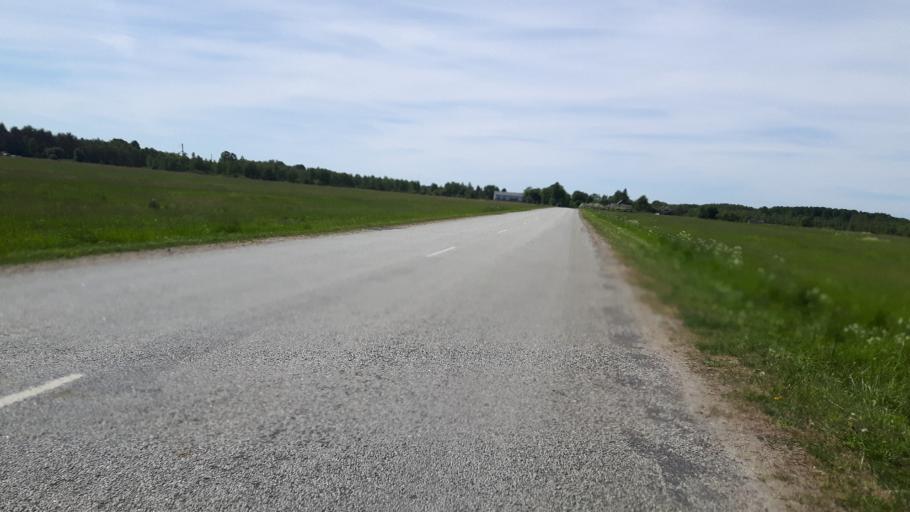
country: EE
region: Harju
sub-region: Kuusalu vald
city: Kuusalu
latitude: 59.4657
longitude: 25.3220
